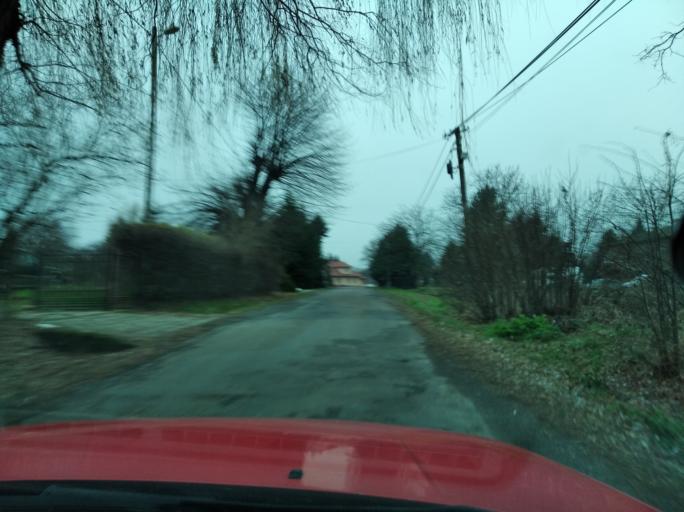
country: PL
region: Subcarpathian Voivodeship
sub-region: Powiat jaroslawski
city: Pawlosiow
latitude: 50.0154
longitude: 22.6376
